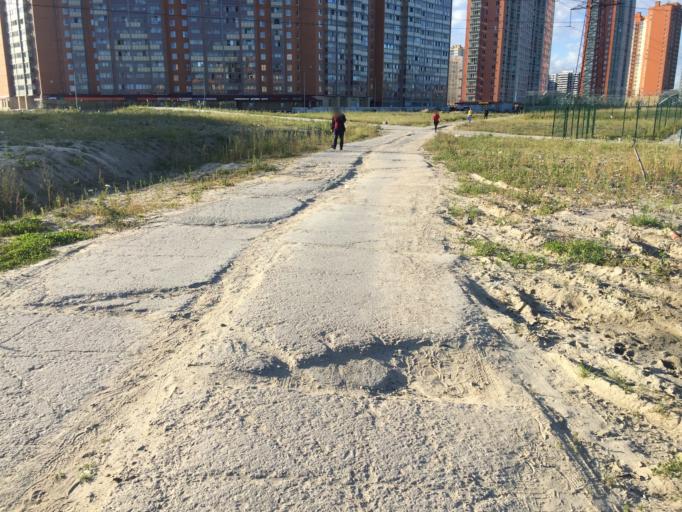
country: RU
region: Leningrad
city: Murino
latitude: 60.0550
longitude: 30.4430
